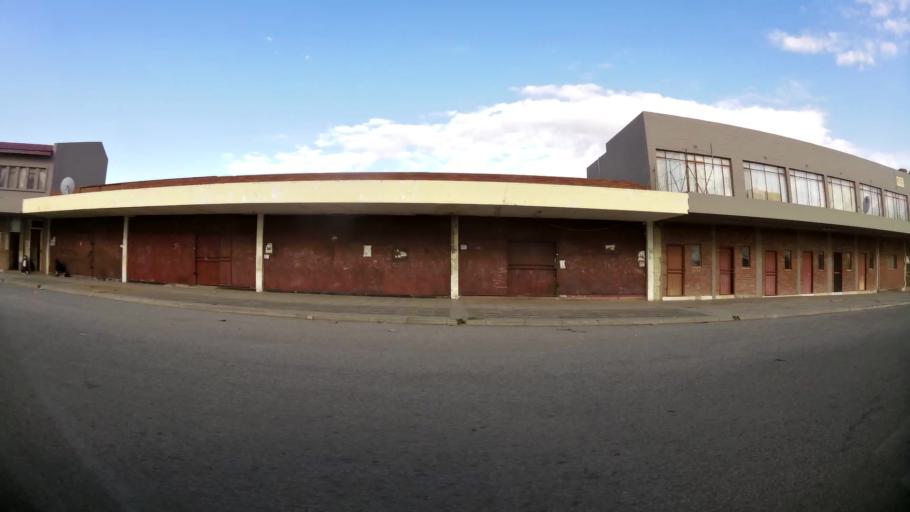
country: ZA
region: Orange Free State
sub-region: Lejweleputswa District Municipality
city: Welkom
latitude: -27.9903
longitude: 26.7130
